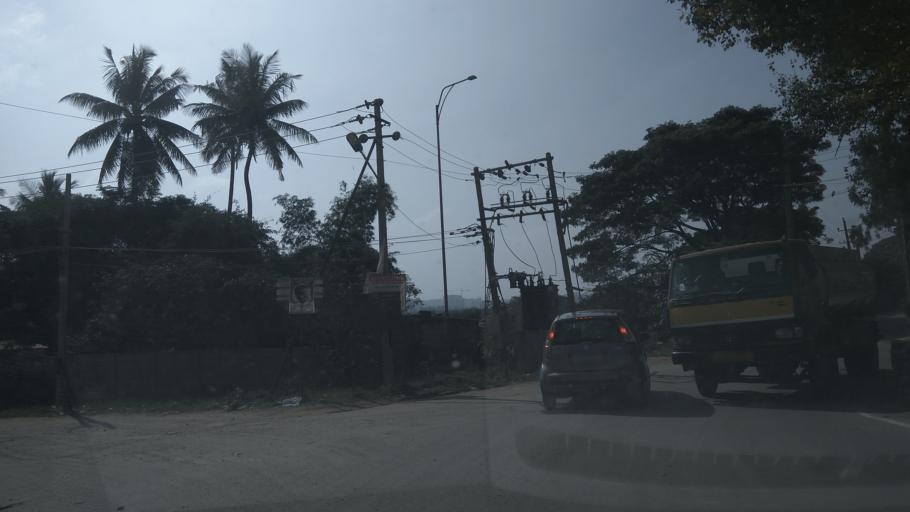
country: IN
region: Karnataka
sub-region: Bangalore Urban
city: Bangalore
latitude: 12.9439
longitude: 77.6804
